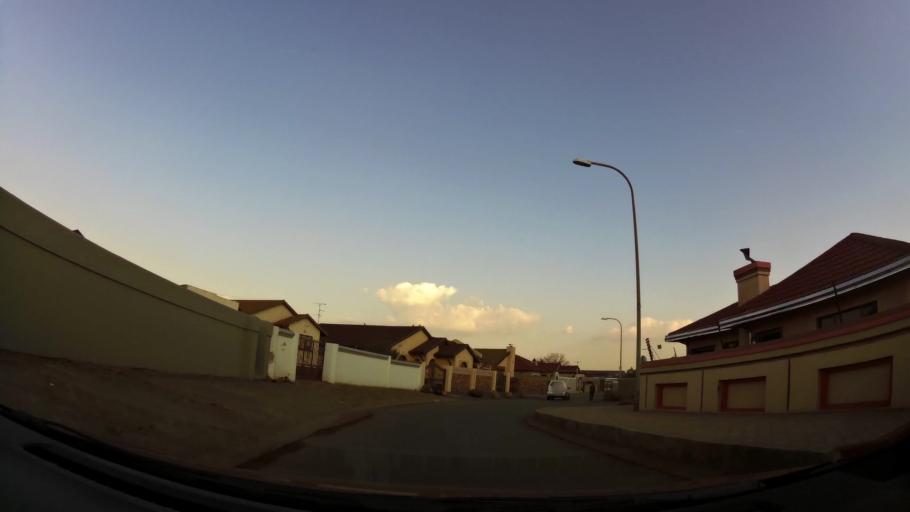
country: ZA
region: Gauteng
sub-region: City of Johannesburg Metropolitan Municipality
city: Soweto
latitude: -26.2193
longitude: 27.8561
